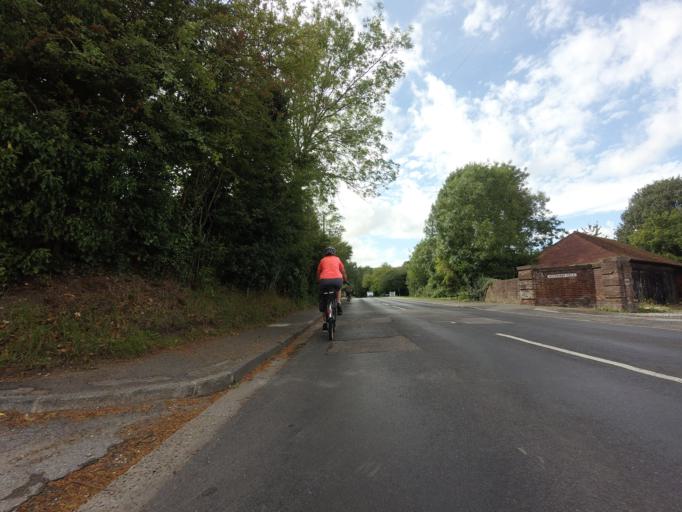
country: GB
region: England
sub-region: Kent
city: Shoreham
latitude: 51.3121
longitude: 0.1735
